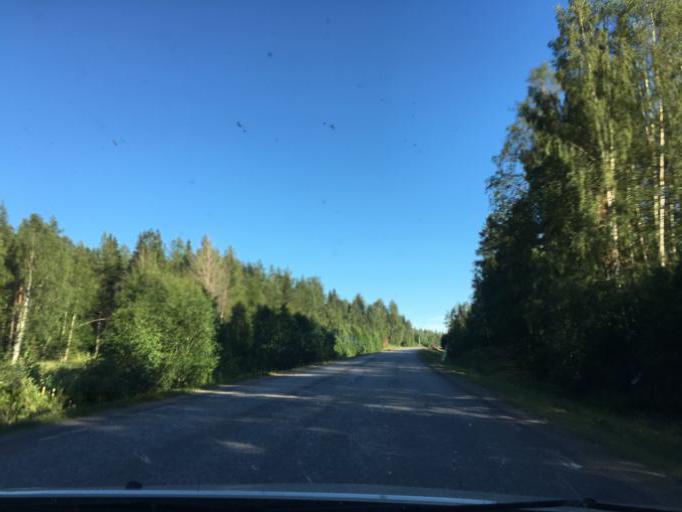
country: SE
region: Norrbotten
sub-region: Kalix Kommun
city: Rolfs
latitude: 65.9132
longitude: 22.9259
